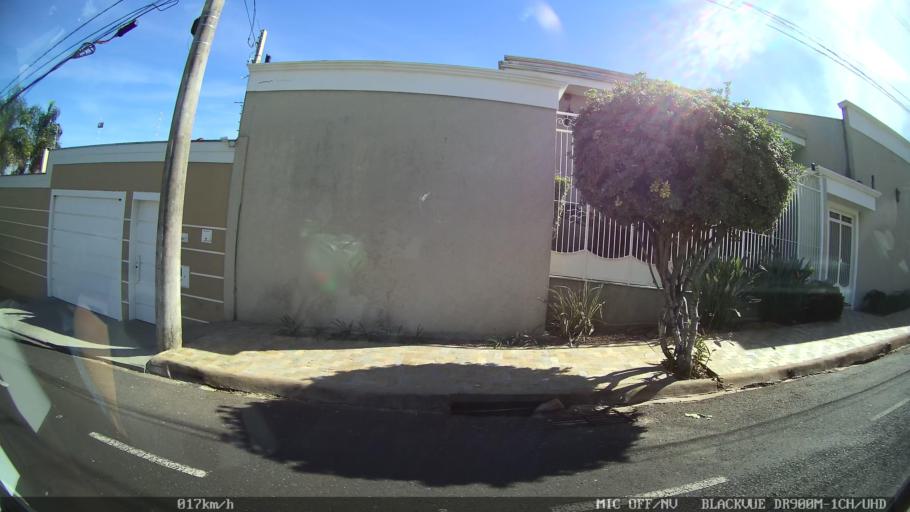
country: BR
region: Sao Paulo
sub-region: Franca
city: Franca
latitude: -20.5500
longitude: -47.4000
